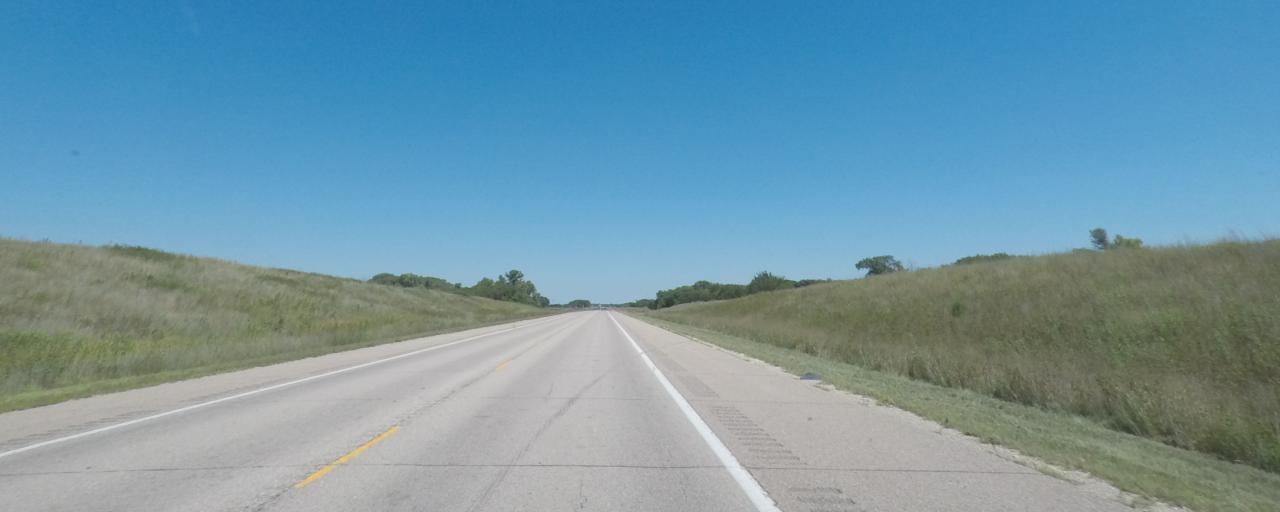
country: US
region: Kansas
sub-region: Marion County
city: Peabody
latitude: 38.1824
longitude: -97.0580
